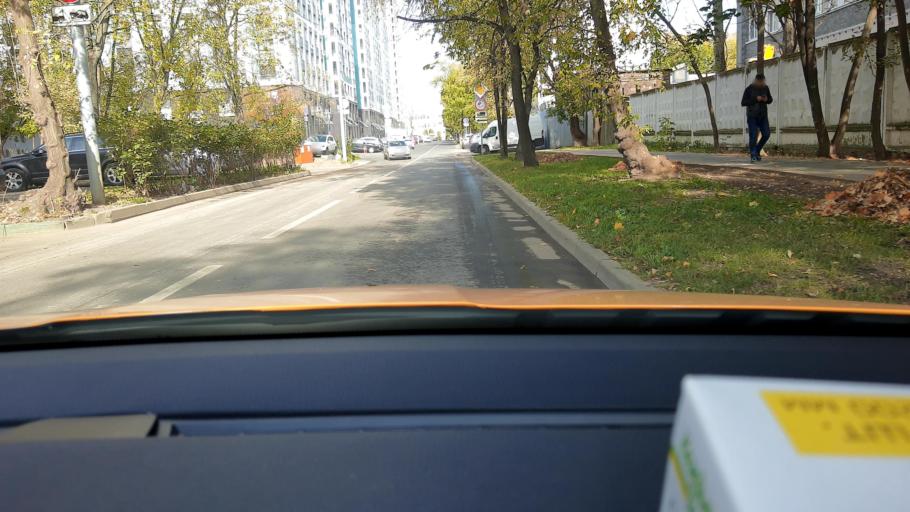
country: RU
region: Moscow
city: Lefortovo
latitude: 55.7739
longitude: 37.7387
